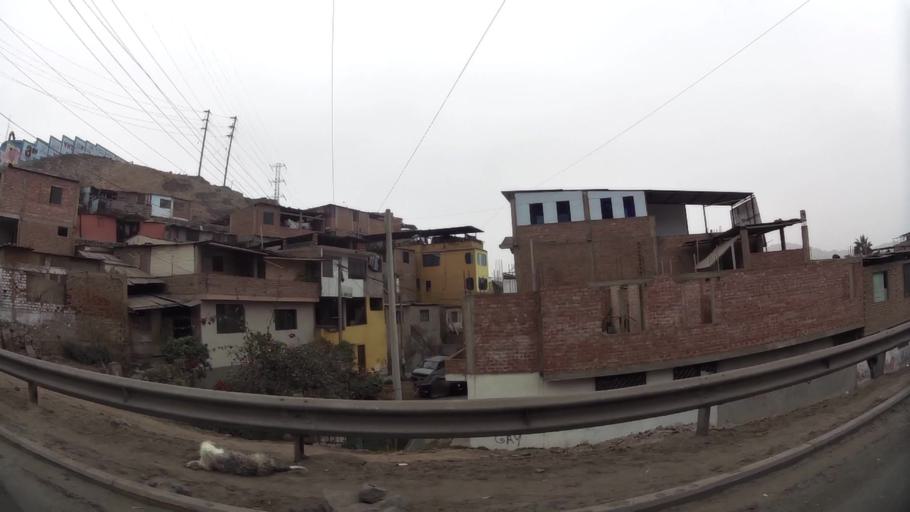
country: PE
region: Lima
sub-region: Lima
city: Surco
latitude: -12.1761
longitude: -76.9414
